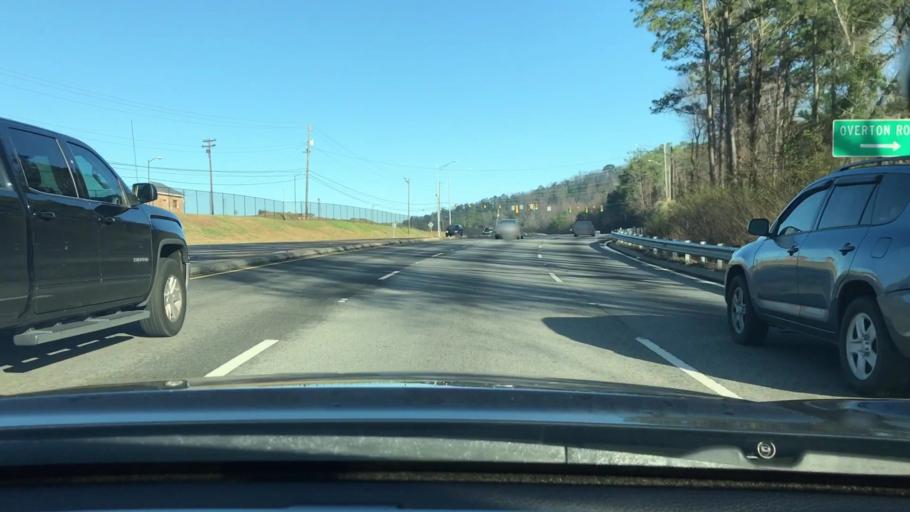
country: US
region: Alabama
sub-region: Jefferson County
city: Cahaba Heights
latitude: 33.4630
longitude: -86.7570
